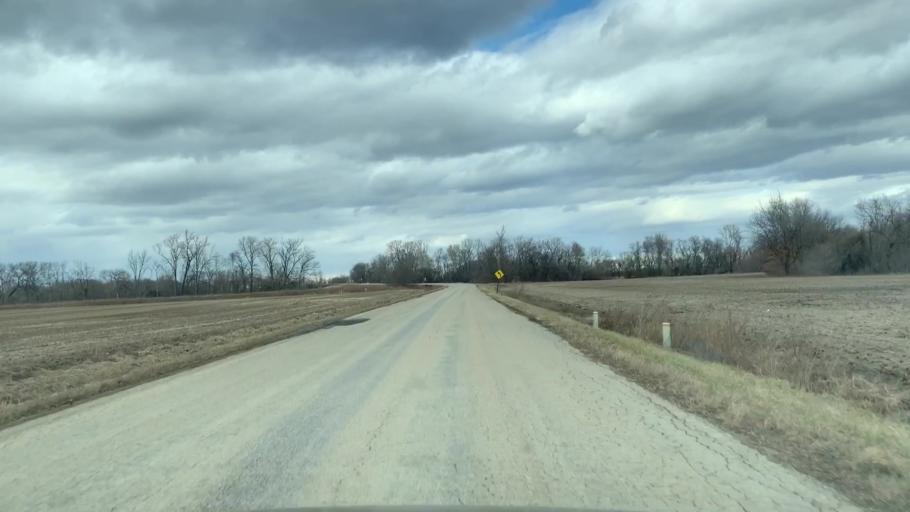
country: US
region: Kansas
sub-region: Allen County
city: Humboldt
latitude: 37.7999
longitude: -95.4705
